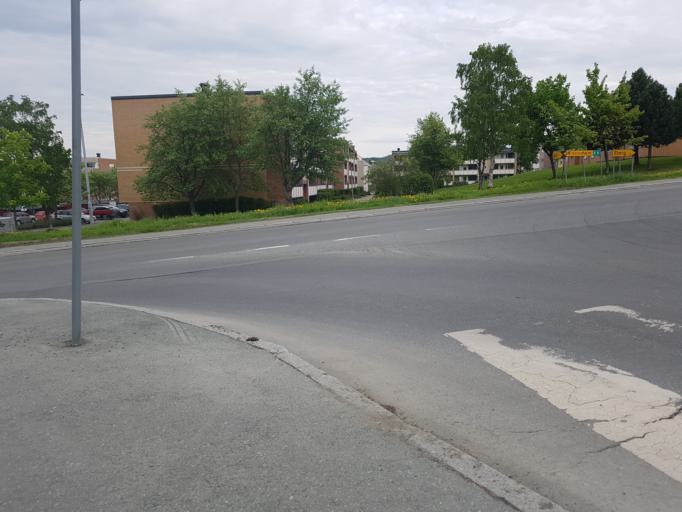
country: NO
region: Sor-Trondelag
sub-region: Trondheim
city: Trondheim
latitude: 63.4274
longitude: 10.4421
